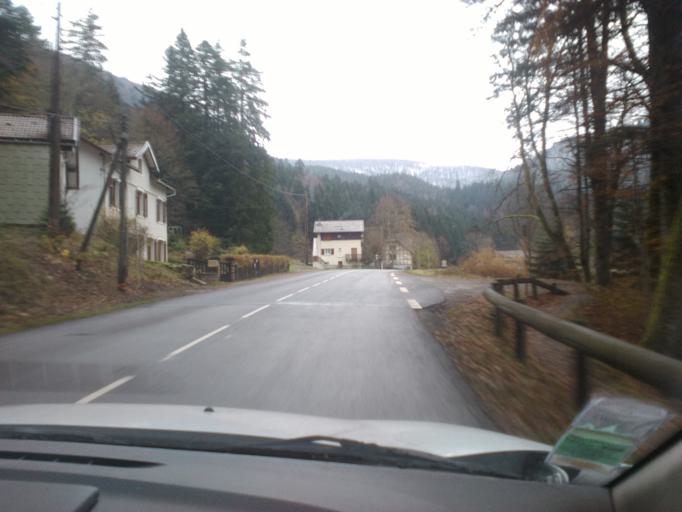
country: FR
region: Lorraine
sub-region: Departement des Vosges
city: Xonrupt-Longemer
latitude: 48.0589
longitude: 6.9845
